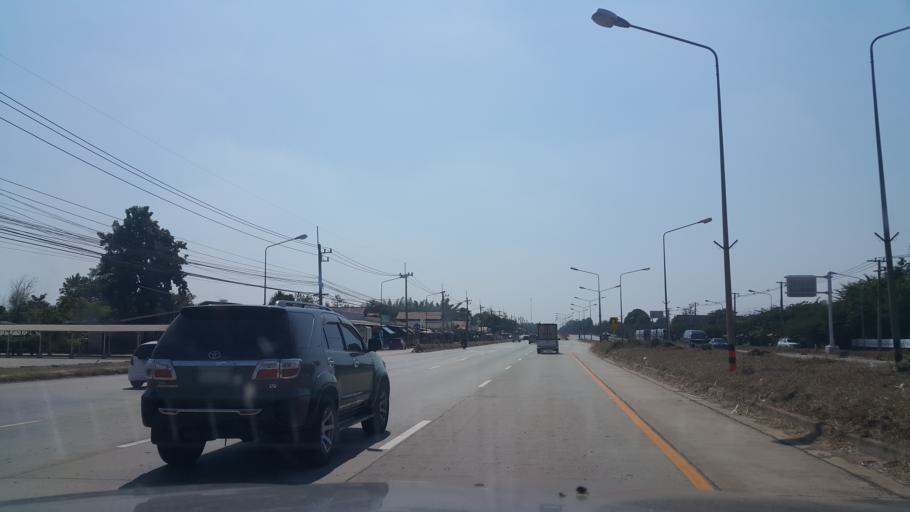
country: TH
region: Changwat Udon Thani
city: Non Sa-at
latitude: 16.8468
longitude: 102.8543
